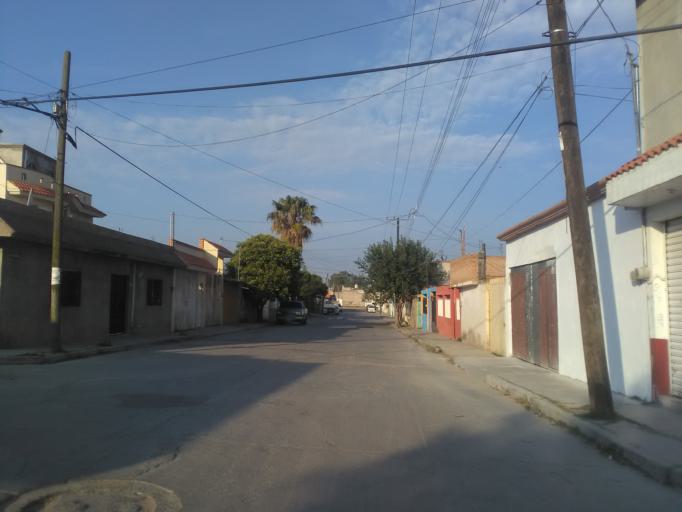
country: MX
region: Durango
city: Victoria de Durango
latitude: 24.0459
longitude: -104.6517
